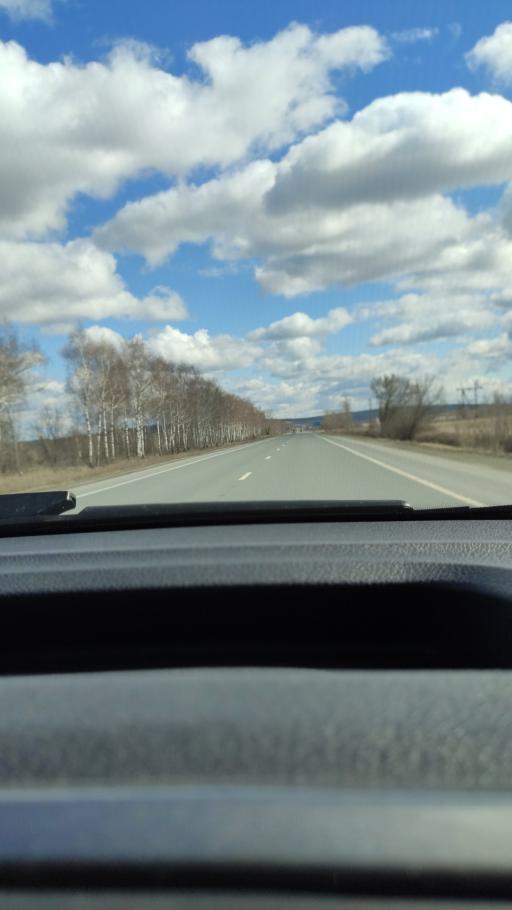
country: RU
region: Samara
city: Kurumoch
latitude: 53.4895
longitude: 49.9877
